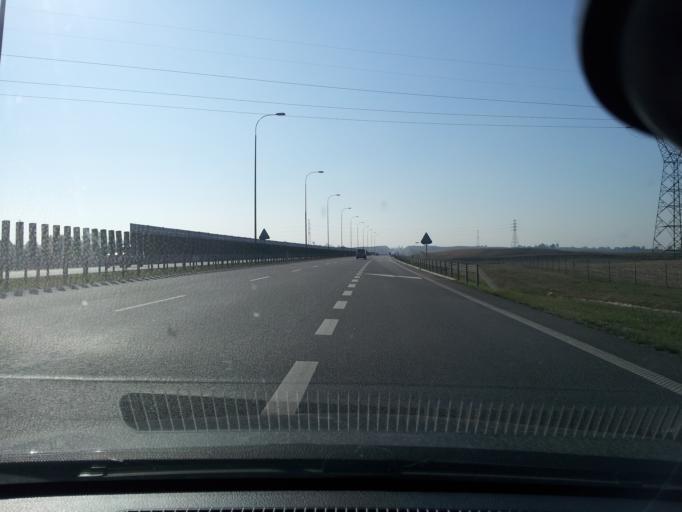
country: PL
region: Kujawsko-Pomorskie
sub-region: Powiat chelminski
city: Lisewo
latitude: 53.3382
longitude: 18.7092
